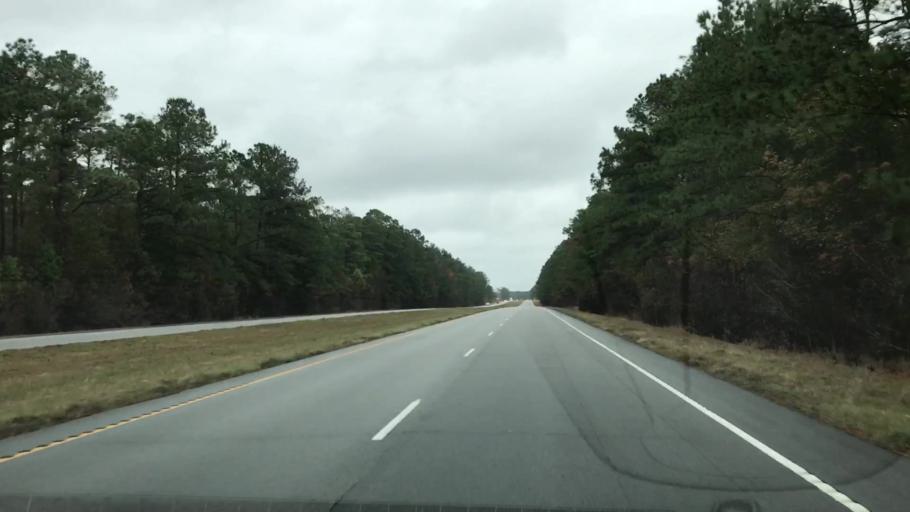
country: US
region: South Carolina
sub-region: Charleston County
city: Awendaw
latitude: 33.1638
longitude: -79.4239
